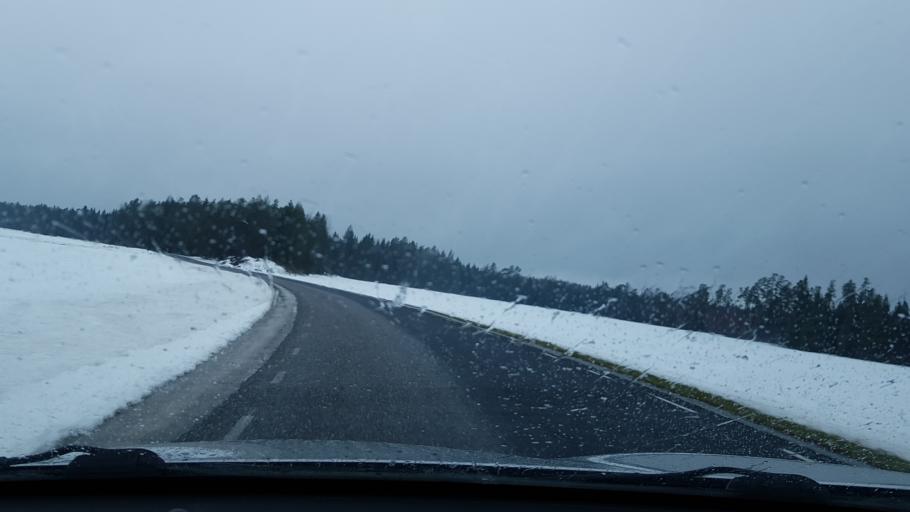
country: EE
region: Harju
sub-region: Saue linn
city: Saue
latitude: 59.1443
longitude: 24.5530
